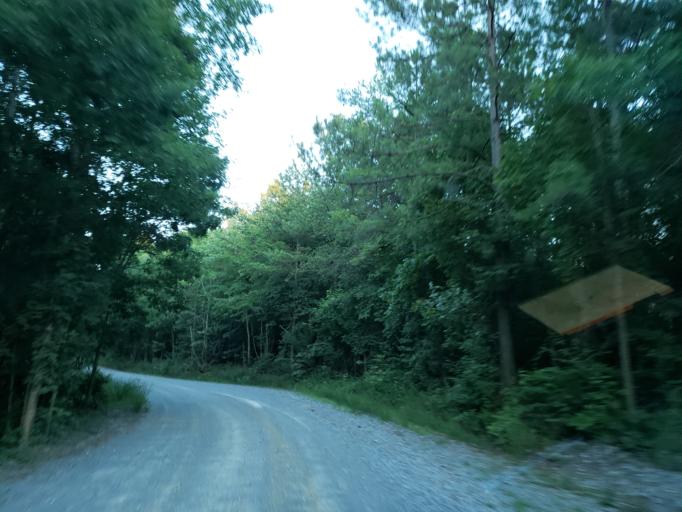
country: US
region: Georgia
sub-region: Bartow County
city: Euharlee
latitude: 34.0648
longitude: -84.8566
